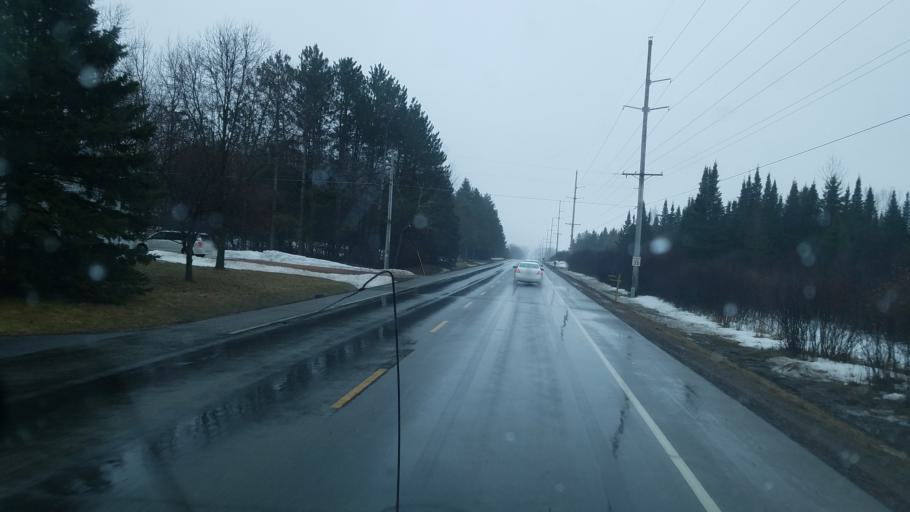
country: US
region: Wisconsin
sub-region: Wood County
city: Marshfield
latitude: 44.6835
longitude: -90.1983
